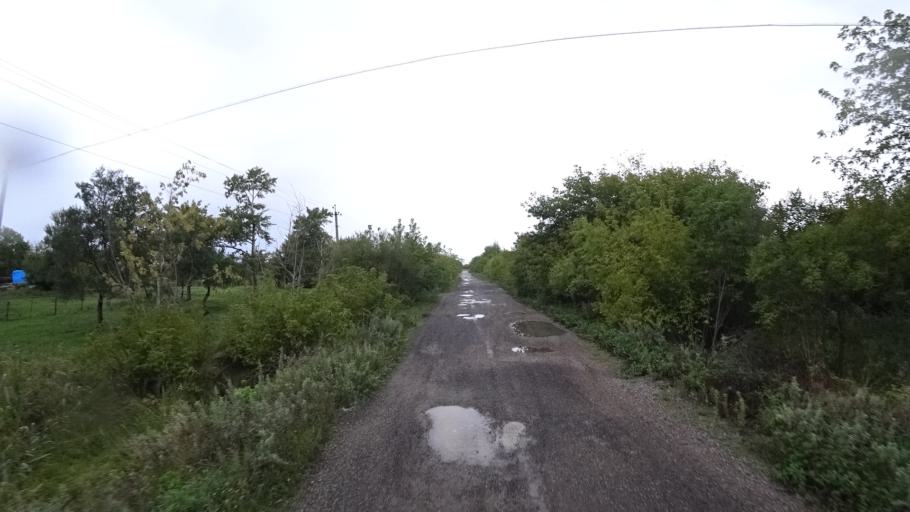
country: RU
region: Primorskiy
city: Chernigovka
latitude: 44.4023
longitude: 132.5316
